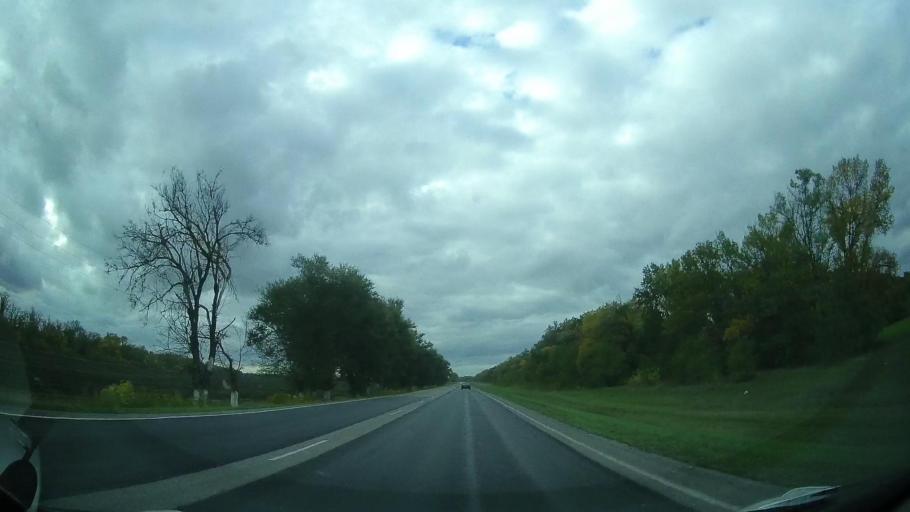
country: RU
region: Rostov
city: Zernograd
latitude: 46.7982
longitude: 40.3695
